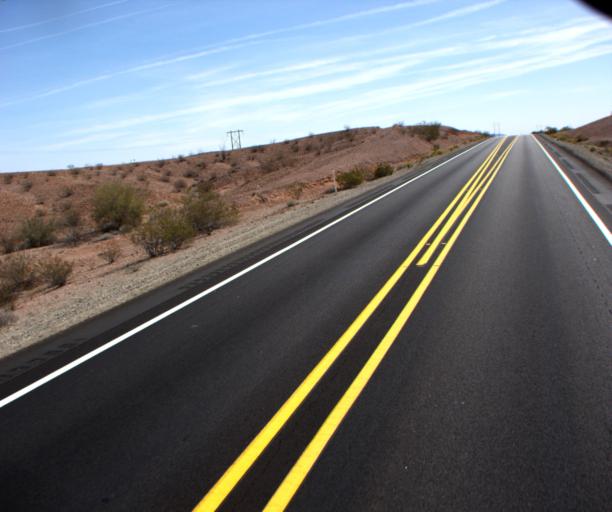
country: US
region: Arizona
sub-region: Yuma County
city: Wellton
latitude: 33.0264
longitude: -114.2877
